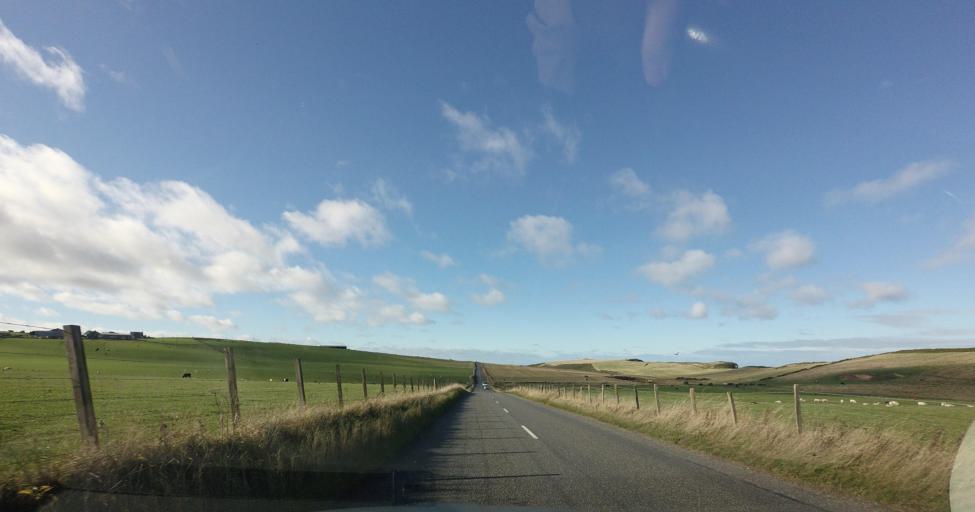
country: GB
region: Scotland
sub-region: Aberdeenshire
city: Macduff
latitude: 57.6639
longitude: -2.3908
